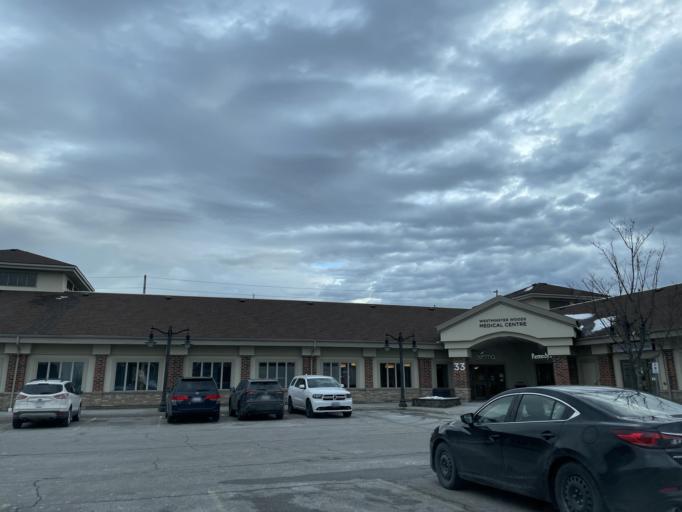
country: CA
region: Ontario
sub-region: Wellington County
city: Guelph
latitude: 43.5026
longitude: -80.1872
